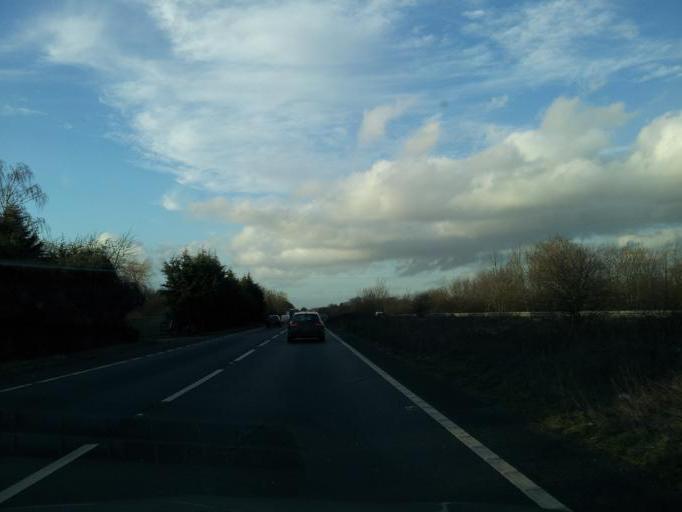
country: GB
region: England
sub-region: District of Rutland
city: Clipsham
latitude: 52.7226
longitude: -0.5960
